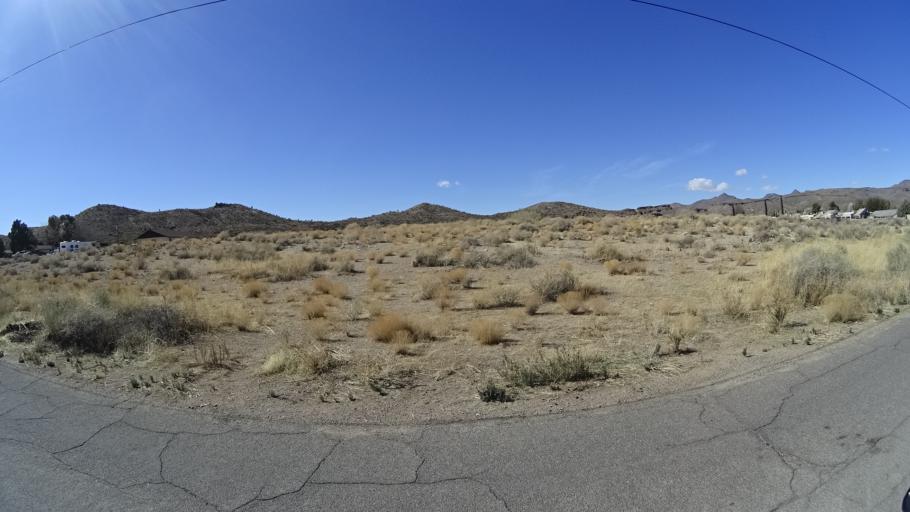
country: US
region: Arizona
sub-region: Mohave County
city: Kingman
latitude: 35.2041
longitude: -114.0399
